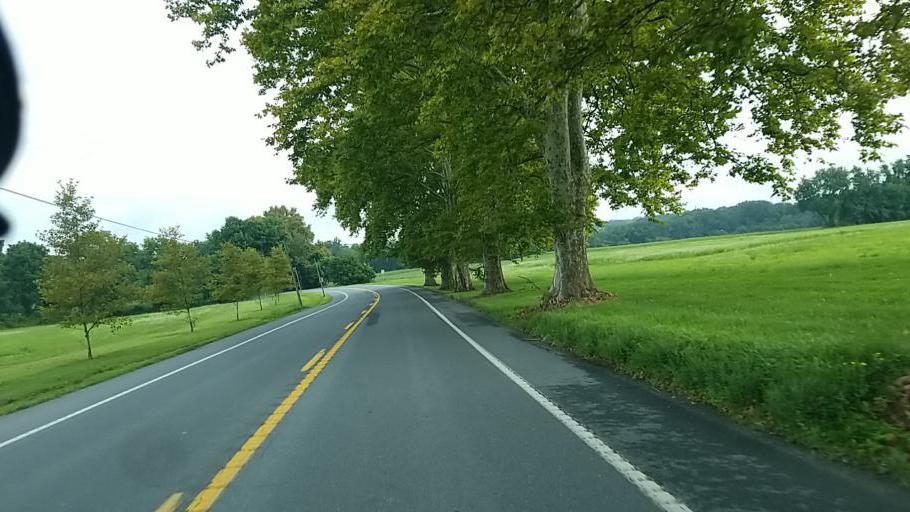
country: US
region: Pennsylvania
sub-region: Dauphin County
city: Matamoras
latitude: 40.4803
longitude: -76.9310
